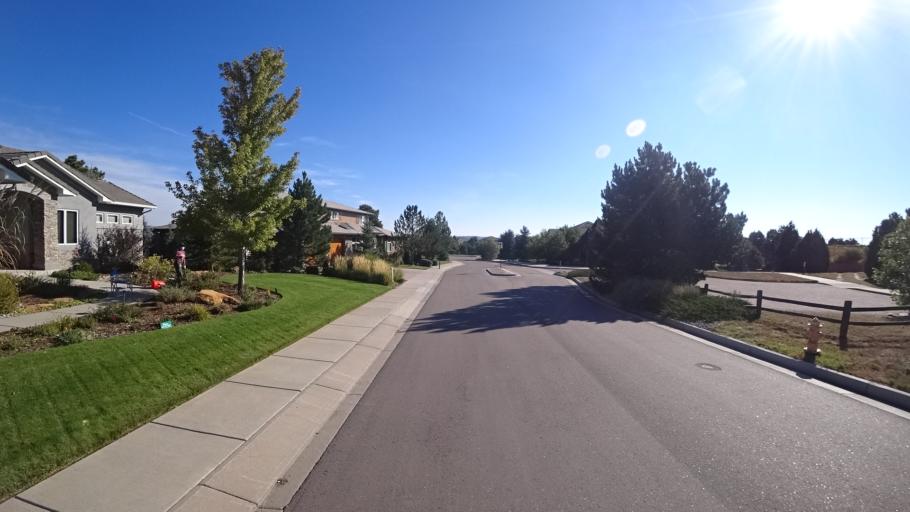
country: US
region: Colorado
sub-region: El Paso County
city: Colorado Springs
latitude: 38.8988
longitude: -104.7971
